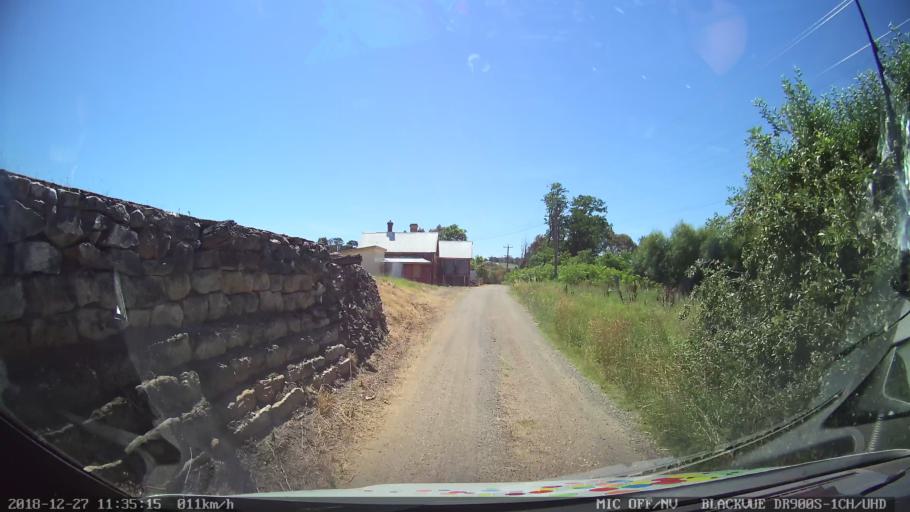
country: AU
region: New South Wales
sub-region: Bathurst Regional
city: Perthville
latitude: -33.5136
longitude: 149.5216
